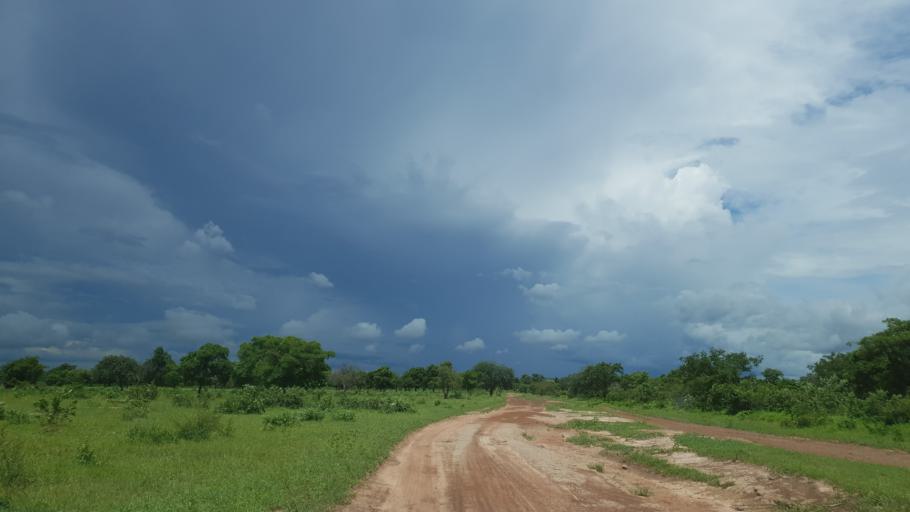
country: ML
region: Koulikoro
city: Kolokani
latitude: 13.5387
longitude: -8.0775
